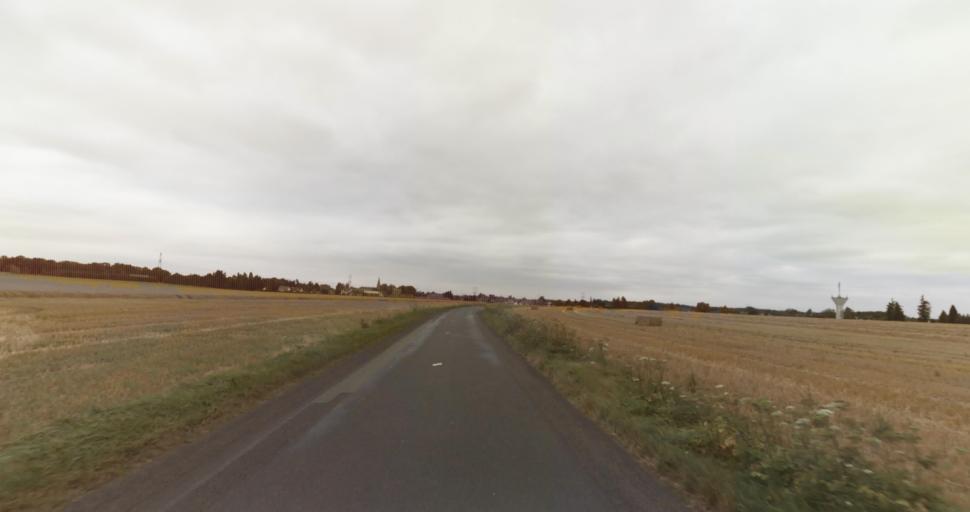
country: FR
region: Haute-Normandie
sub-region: Departement de l'Eure
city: La Couture-Boussey
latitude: 48.9038
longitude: 1.4070
